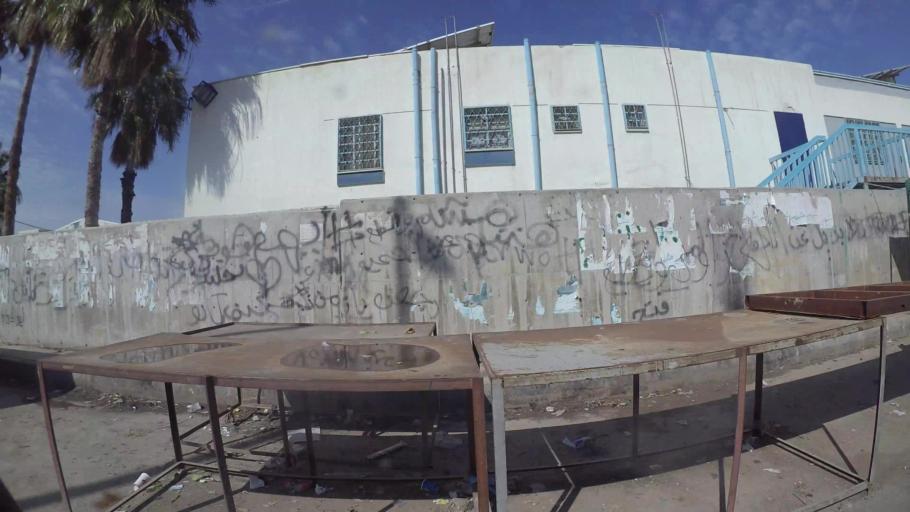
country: JO
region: Amman
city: Al Jubayhah
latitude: 32.0752
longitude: 35.8451
